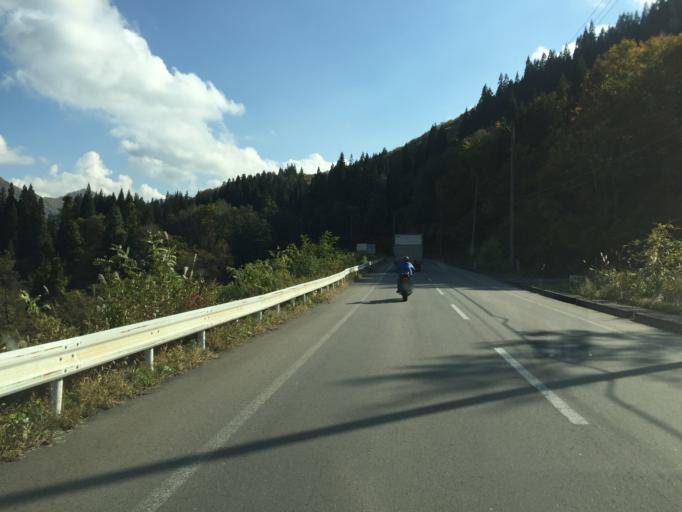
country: JP
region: Yamagata
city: Yonezawa
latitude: 37.8551
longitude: 139.9900
